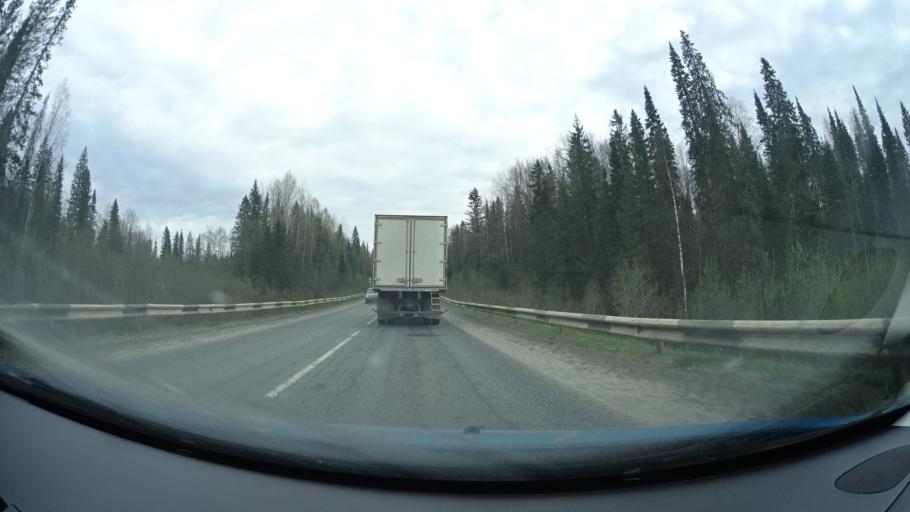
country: RU
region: Perm
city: Yugo-Kamskiy
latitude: 57.5930
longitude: 55.6644
